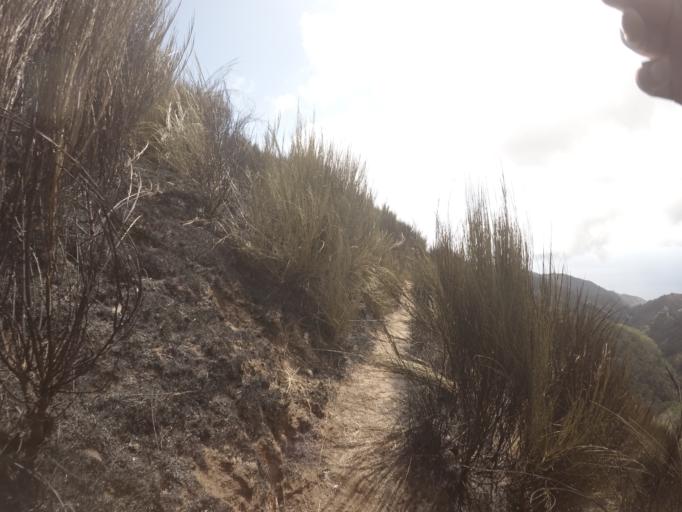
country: PT
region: Madeira
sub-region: Camara de Lobos
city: Curral das Freiras
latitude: 32.7100
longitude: -17.0026
